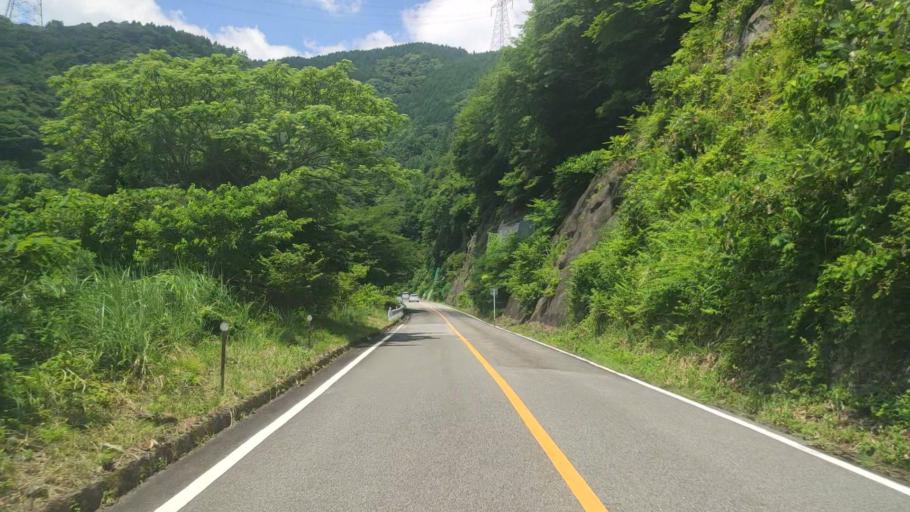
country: JP
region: Gifu
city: Tarui
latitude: 35.3828
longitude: 136.4517
